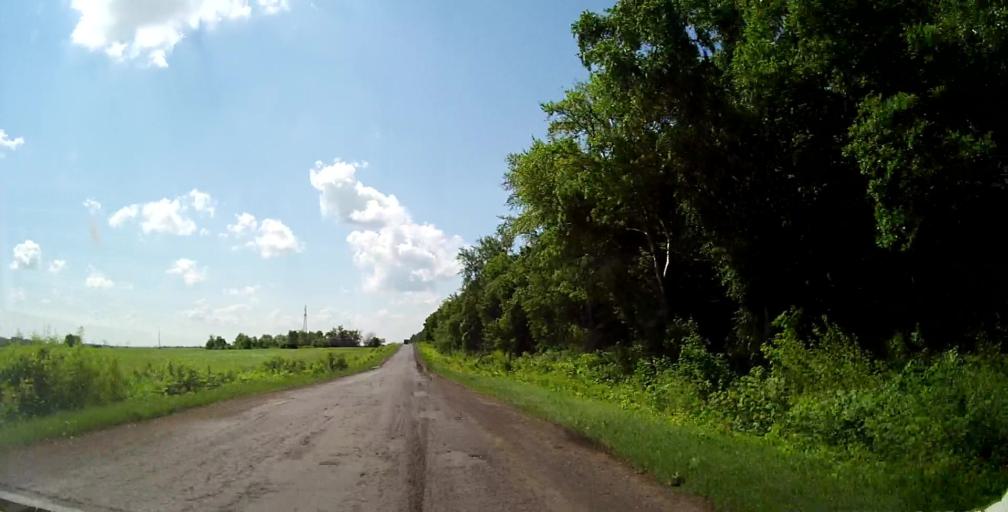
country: RU
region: Lipetsk
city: Chaplygin
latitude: 53.2957
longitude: 39.9556
